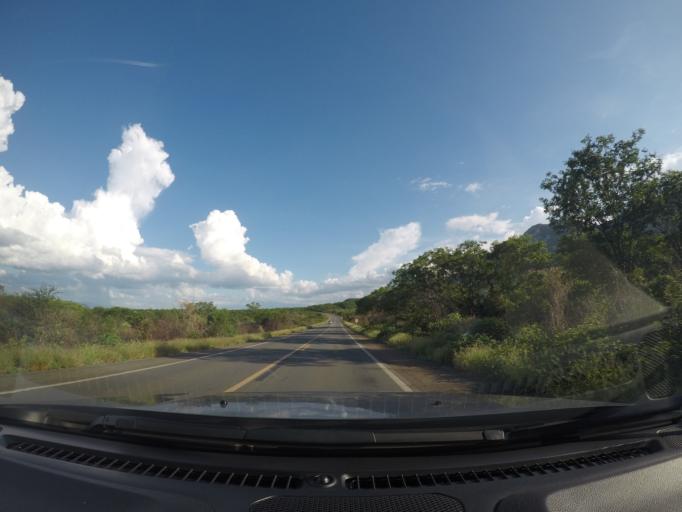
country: BR
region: Bahia
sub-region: Oliveira Dos Brejinhos
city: Oliveira dos Brejinhos
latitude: -12.0635
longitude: -42.9603
